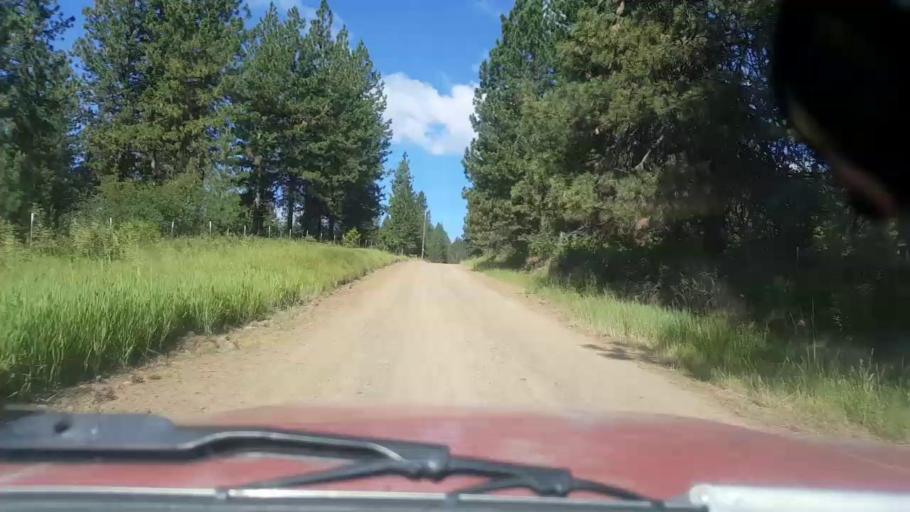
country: US
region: Washington
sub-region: Garfield County
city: Pomeroy
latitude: 46.0370
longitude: -117.4376
